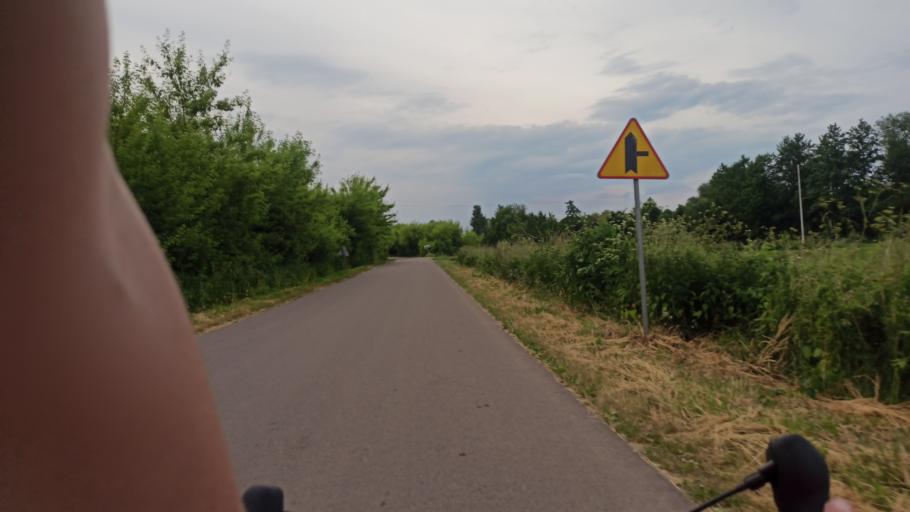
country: PL
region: Subcarpathian Voivodeship
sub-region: Powiat jaroslawski
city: Radymno
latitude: 49.9164
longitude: 22.8028
